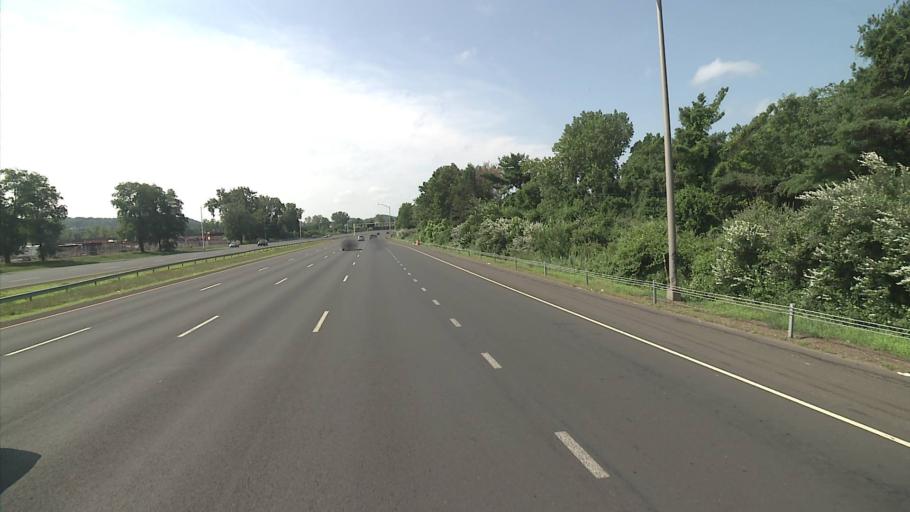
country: US
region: Connecticut
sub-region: New Haven County
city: North Haven
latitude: 41.3465
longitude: -72.8686
